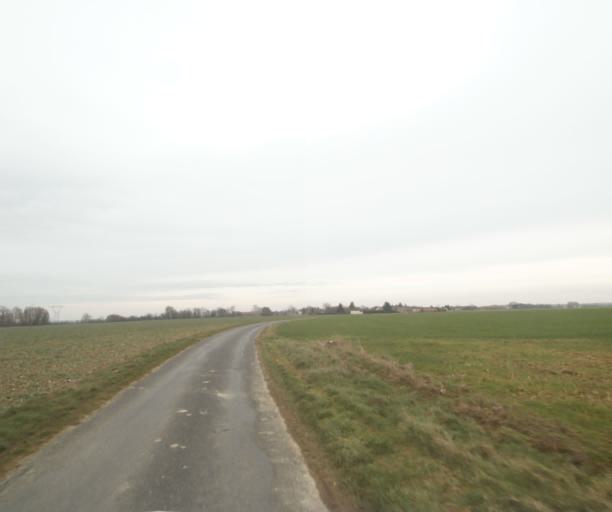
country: FR
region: Champagne-Ardenne
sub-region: Departement de la Haute-Marne
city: Villiers-en-Lieu
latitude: 48.6335
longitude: 4.8259
